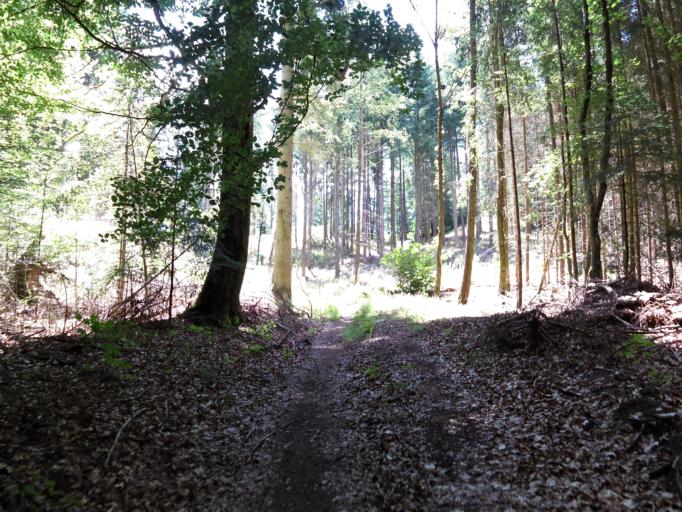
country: DE
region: Rheinland-Pfalz
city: Altleiningen
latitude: 49.4721
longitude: 8.0634
